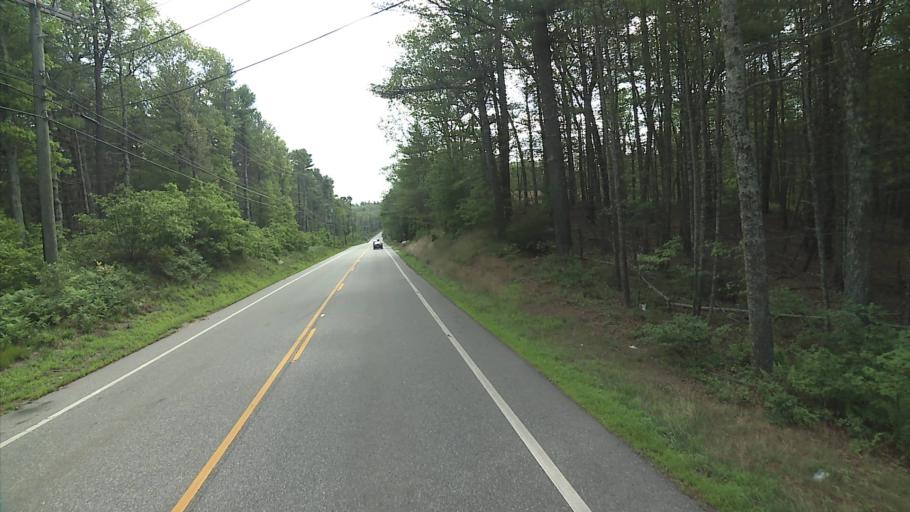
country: US
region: Connecticut
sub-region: Windham County
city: Plainfield
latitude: 41.5754
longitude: -71.8448
